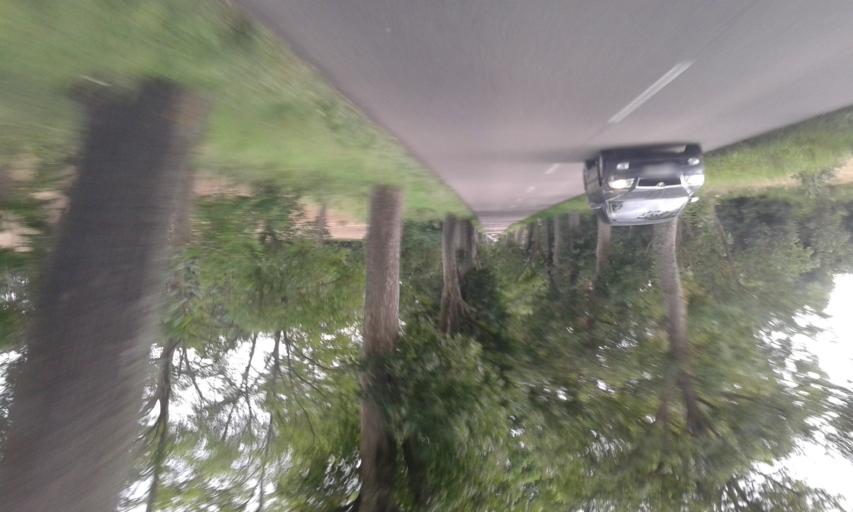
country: PL
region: West Pomeranian Voivodeship
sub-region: Powiat szczecinecki
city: Barwice
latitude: 53.7519
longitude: 16.3151
